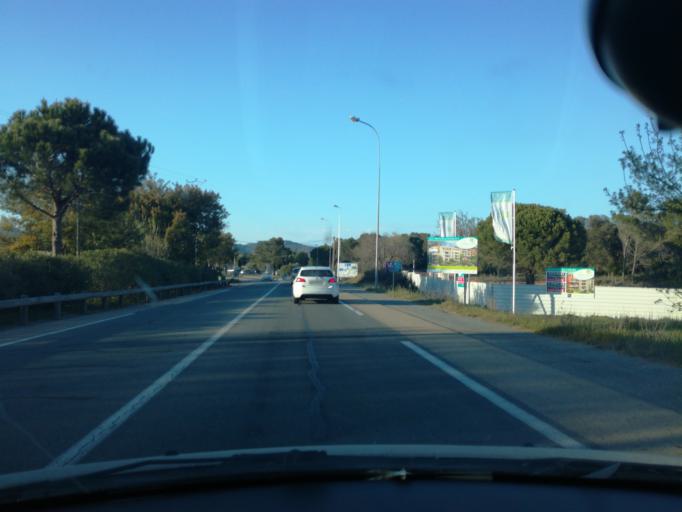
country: FR
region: Provence-Alpes-Cote d'Azur
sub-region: Departement du Var
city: Frejus
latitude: 43.4690
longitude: 6.7445
